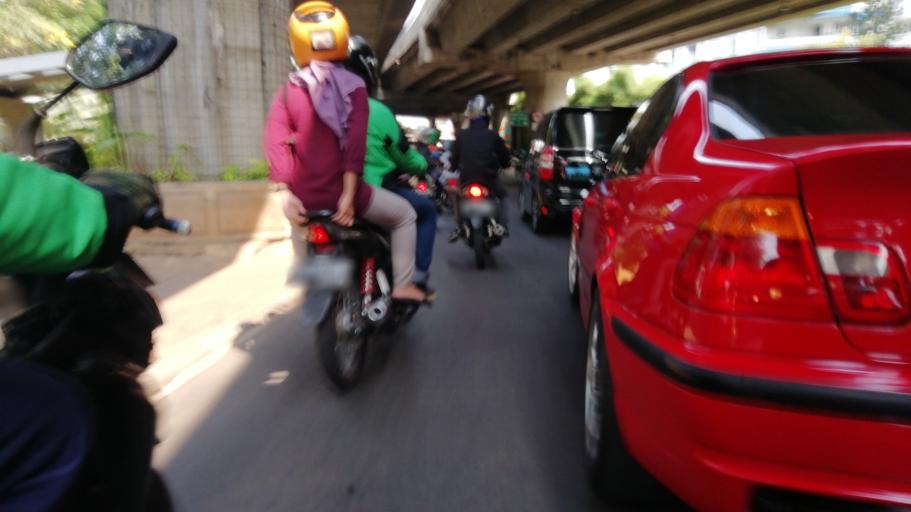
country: ID
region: Jakarta Raya
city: Jakarta
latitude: -6.2492
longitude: 106.8080
